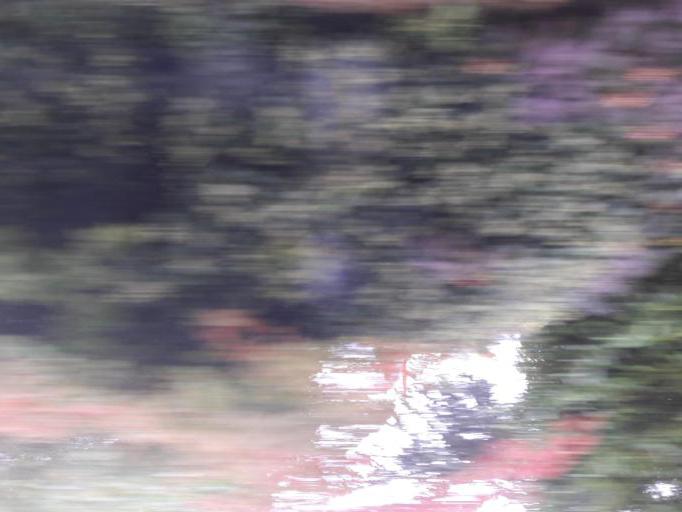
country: CH
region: Lucerne
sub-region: Lucerne-Land District
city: Meggen
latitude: 47.0461
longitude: 8.3762
